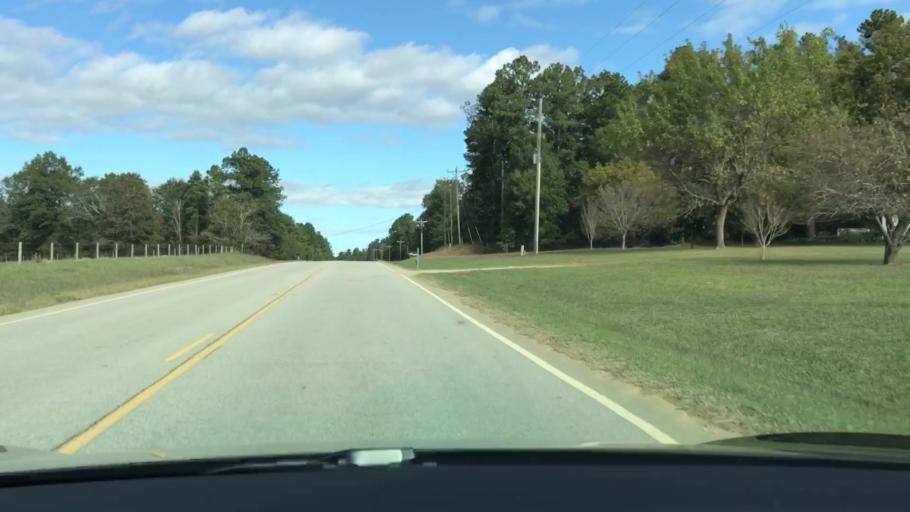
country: US
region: Georgia
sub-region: Jefferson County
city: Louisville
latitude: 33.0830
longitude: -82.4134
